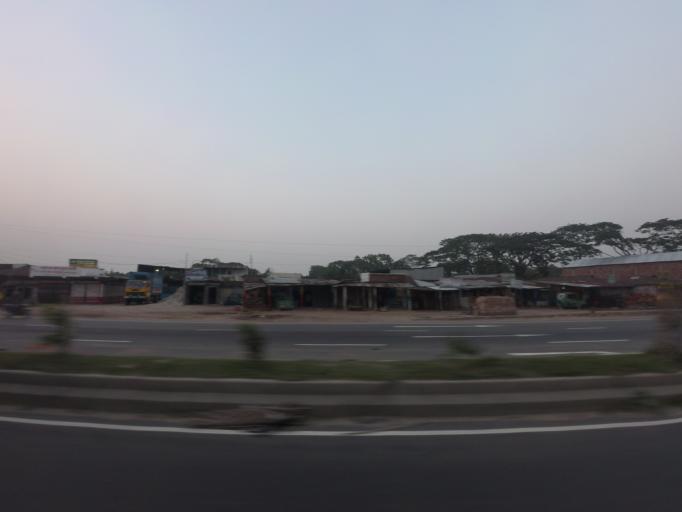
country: BD
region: Chittagong
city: Comilla
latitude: 23.4875
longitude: 91.0162
